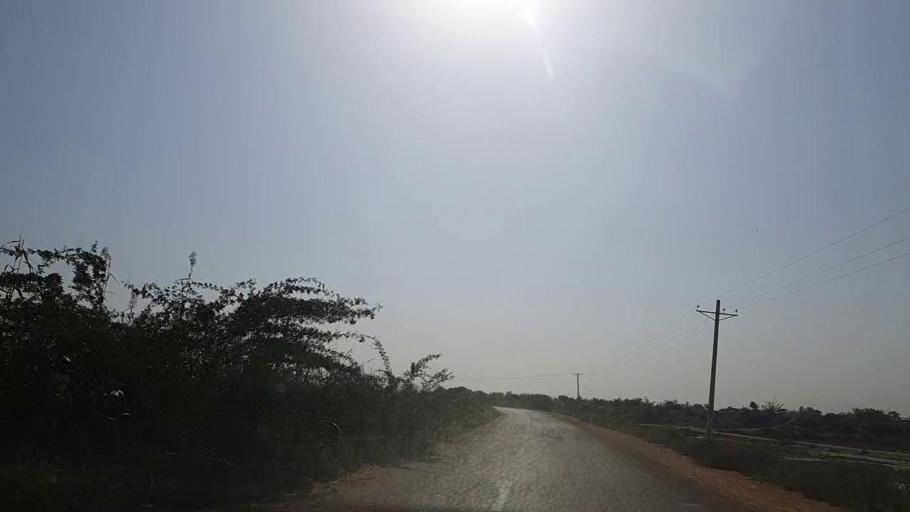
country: PK
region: Sindh
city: Jati
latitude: 24.4580
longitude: 68.2660
